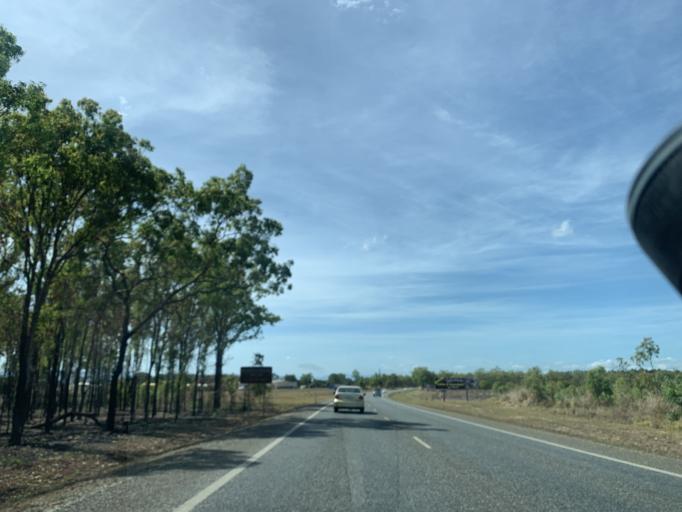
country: AU
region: Queensland
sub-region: Tablelands
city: Mareeba
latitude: -17.0757
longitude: 145.4356
